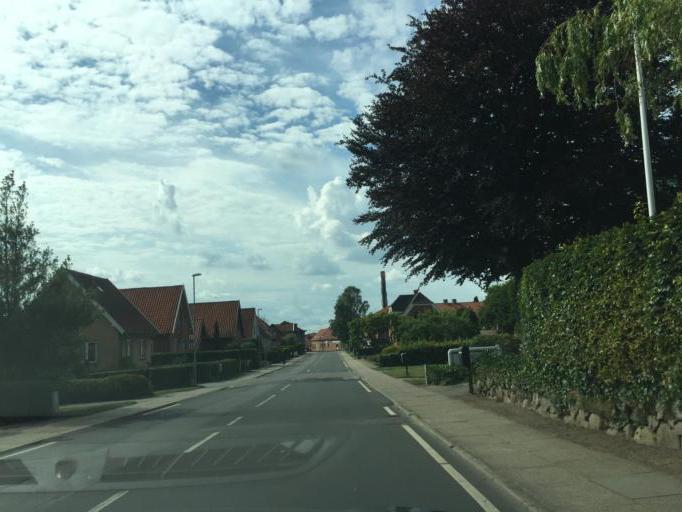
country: DK
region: South Denmark
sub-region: Kerteminde Kommune
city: Langeskov
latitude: 55.3579
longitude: 10.5933
